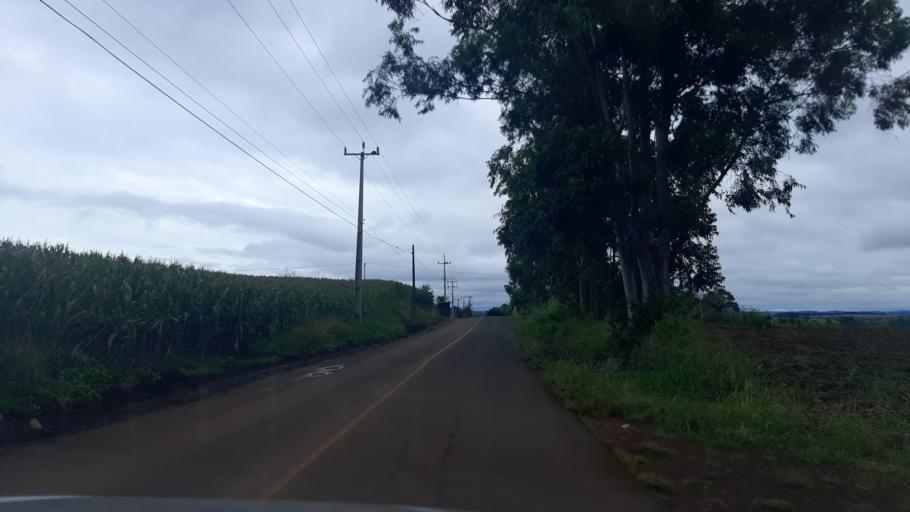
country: BR
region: Parana
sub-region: Ampere
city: Ampere
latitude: -26.0382
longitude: -53.5046
